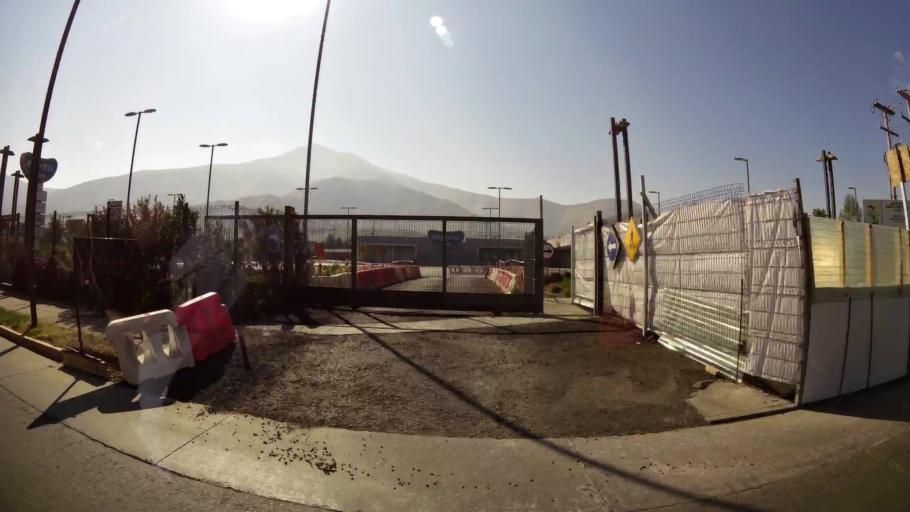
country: CL
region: Santiago Metropolitan
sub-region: Provincia de Chacabuco
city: Chicureo Abajo
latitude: -33.3532
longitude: -70.6704
